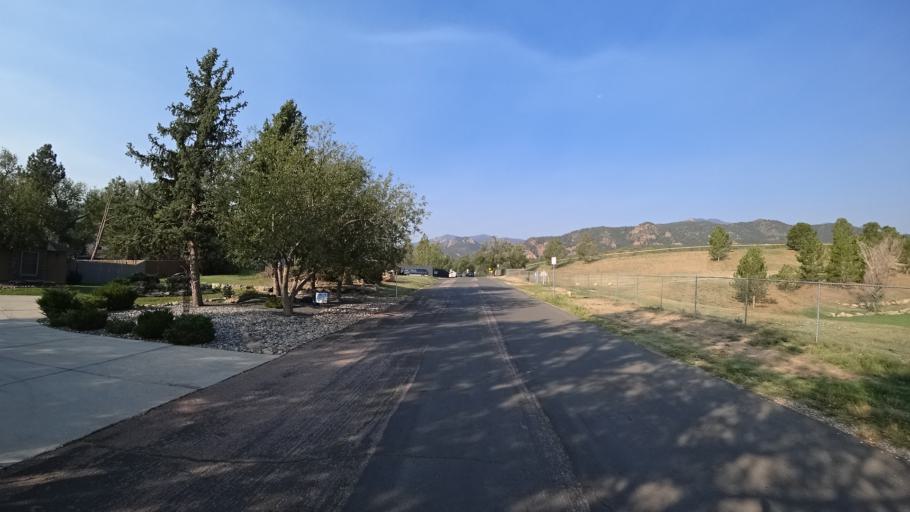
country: US
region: Colorado
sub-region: El Paso County
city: Colorado Springs
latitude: 38.8012
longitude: -104.8554
